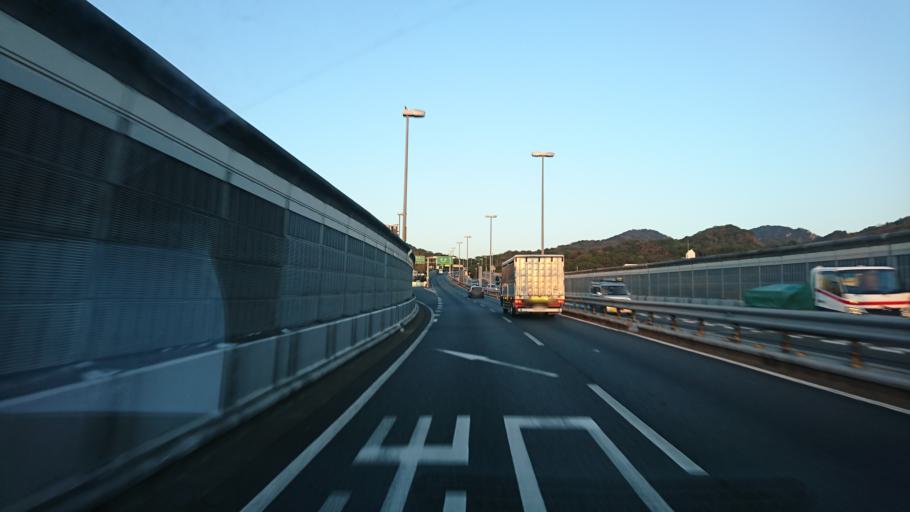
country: JP
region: Hyogo
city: Kobe
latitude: 34.6515
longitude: 135.1254
